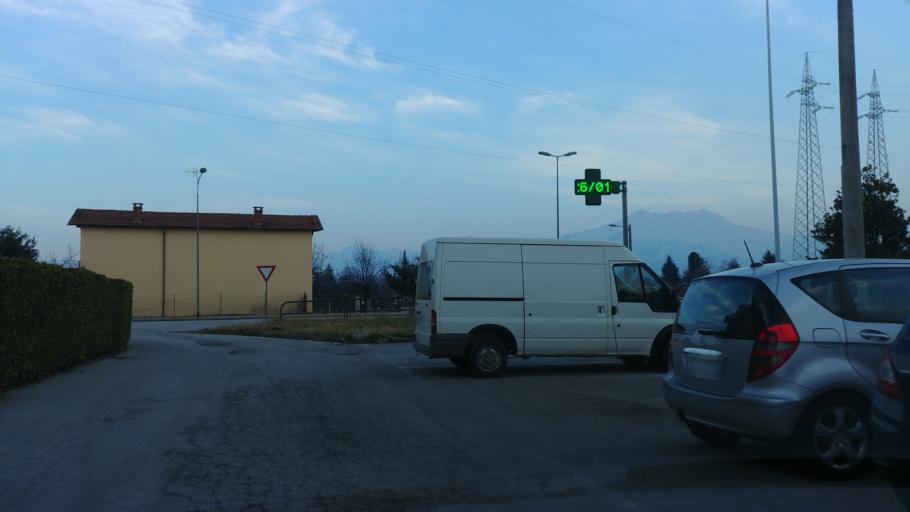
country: IT
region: Piedmont
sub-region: Provincia di Cuneo
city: Cuneo
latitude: 44.3995
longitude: 7.5331
